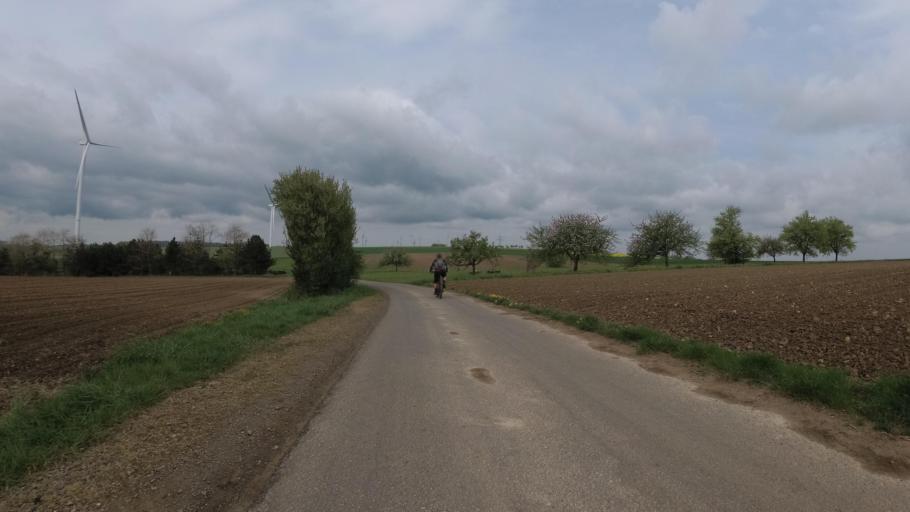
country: DE
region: Saarland
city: Orscholz
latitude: 49.4366
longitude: 6.5232
